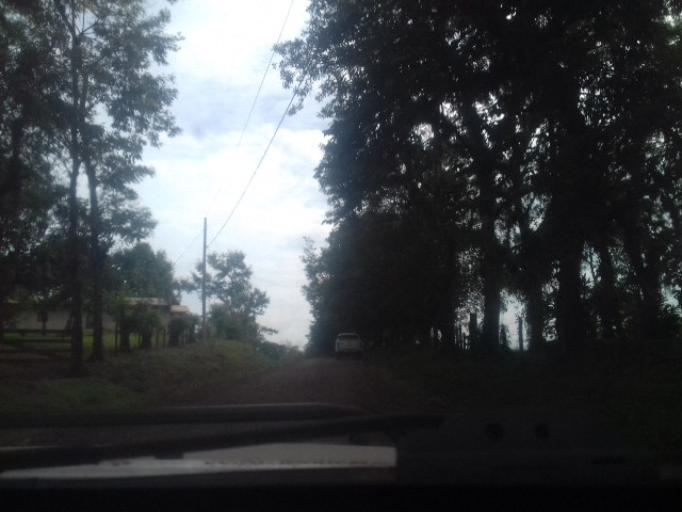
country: NI
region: Atlantico Norte (RAAN)
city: Waslala
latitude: 13.3999
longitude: -85.3228
